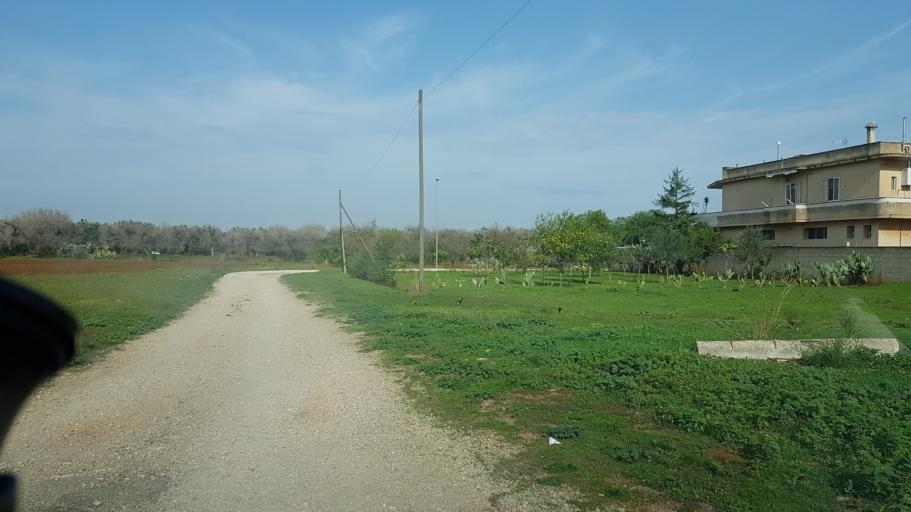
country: IT
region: Apulia
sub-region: Provincia di Brindisi
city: Cellino San Marco
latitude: 40.4779
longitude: 17.9747
